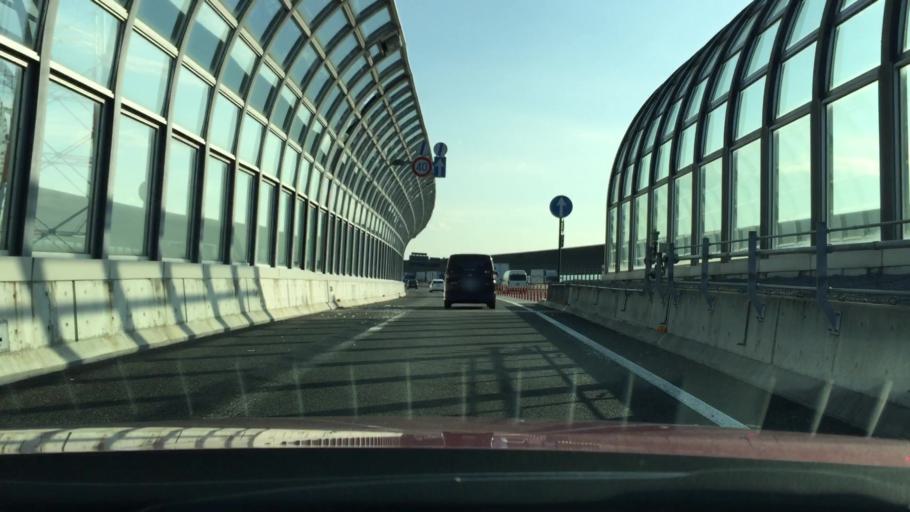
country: JP
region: Osaka
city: Daitocho
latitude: 34.7200
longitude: 135.5975
